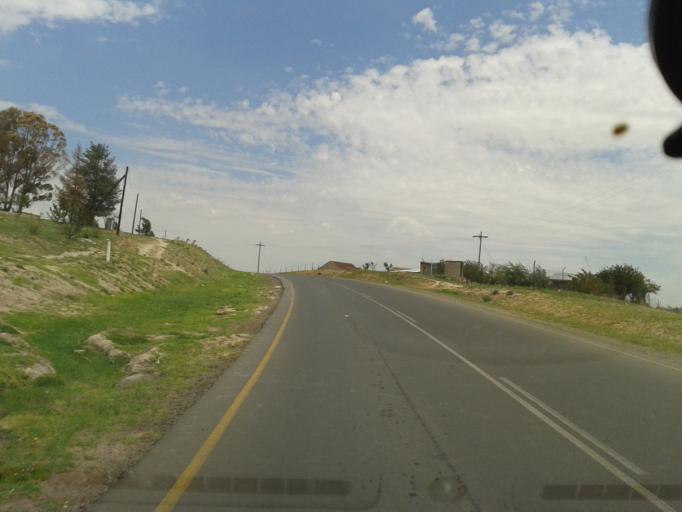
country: LS
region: Maseru
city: Maseru
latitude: -29.3509
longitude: 27.6573
